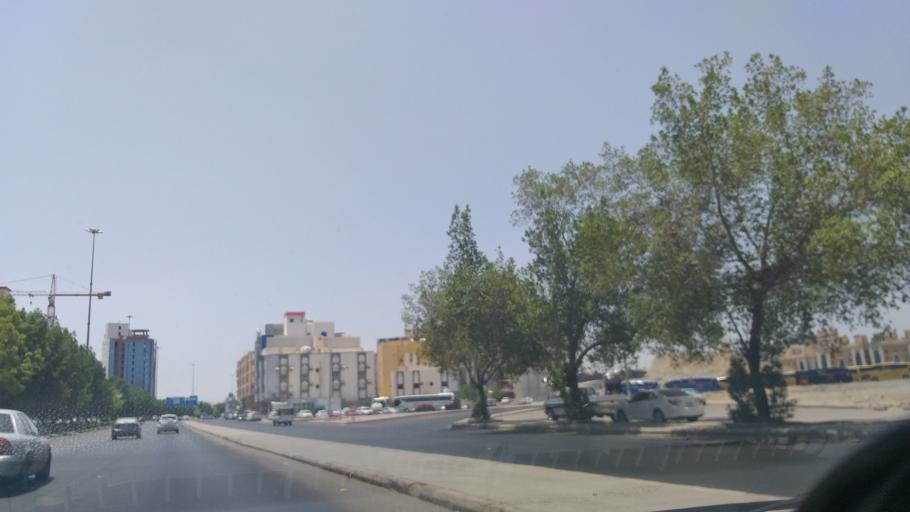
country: SA
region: Makkah
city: Mecca
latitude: 21.3965
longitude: 39.7943
